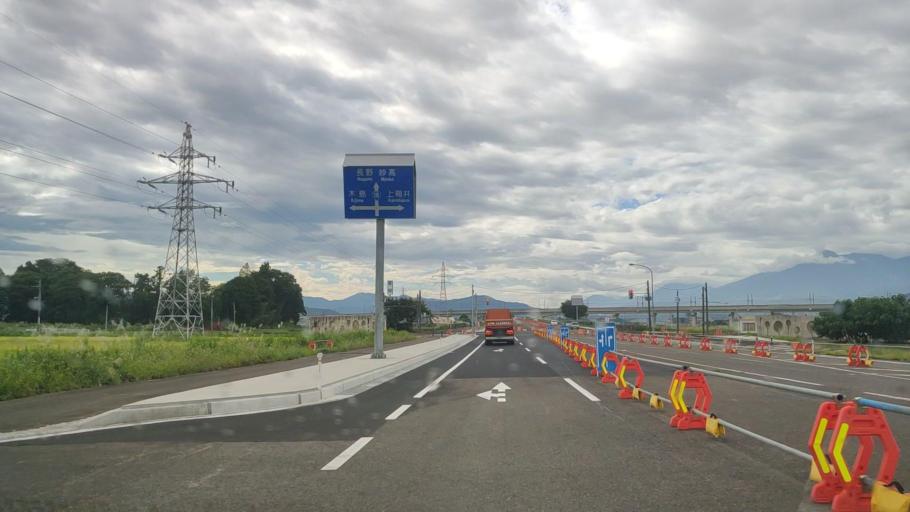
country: JP
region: Niigata
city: Joetsu
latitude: 37.0737
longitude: 138.2649
